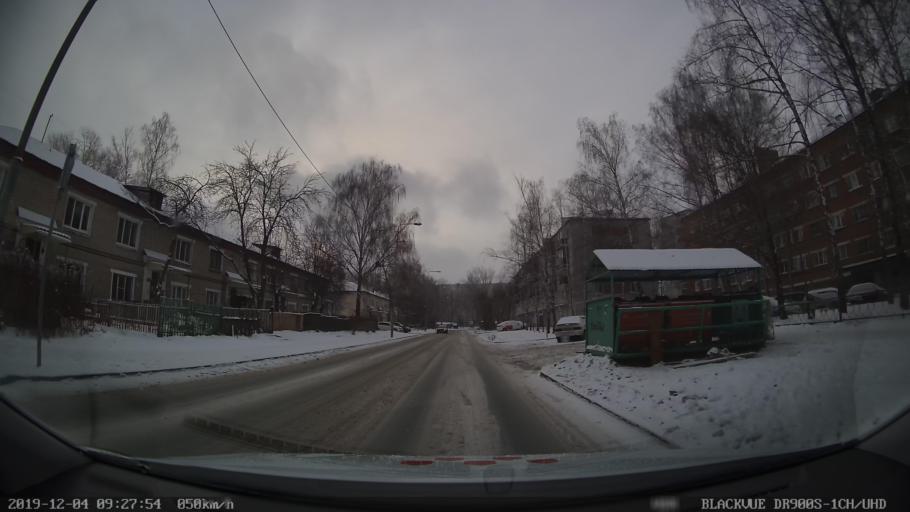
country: RU
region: Tatarstan
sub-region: Gorod Kazan'
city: Kazan
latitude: 55.8411
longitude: 49.1080
